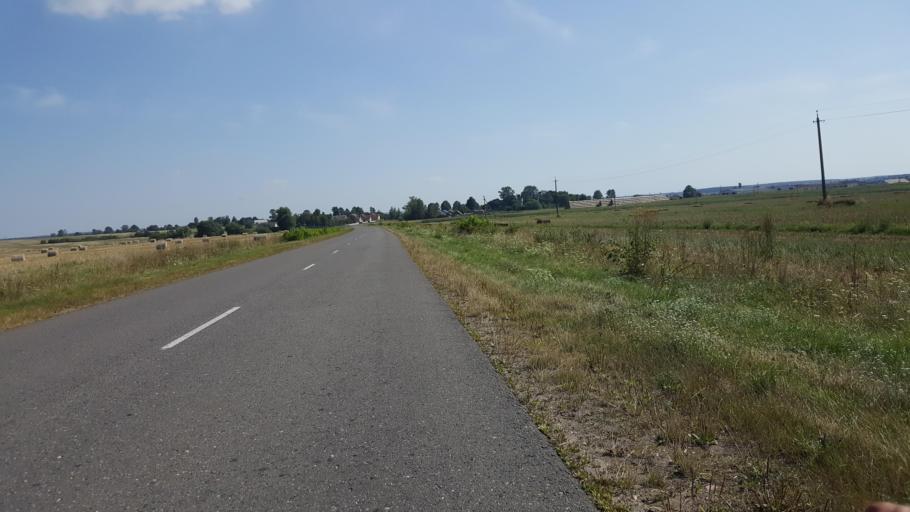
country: BY
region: Brest
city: Kamyanyets
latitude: 52.4371
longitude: 23.7458
